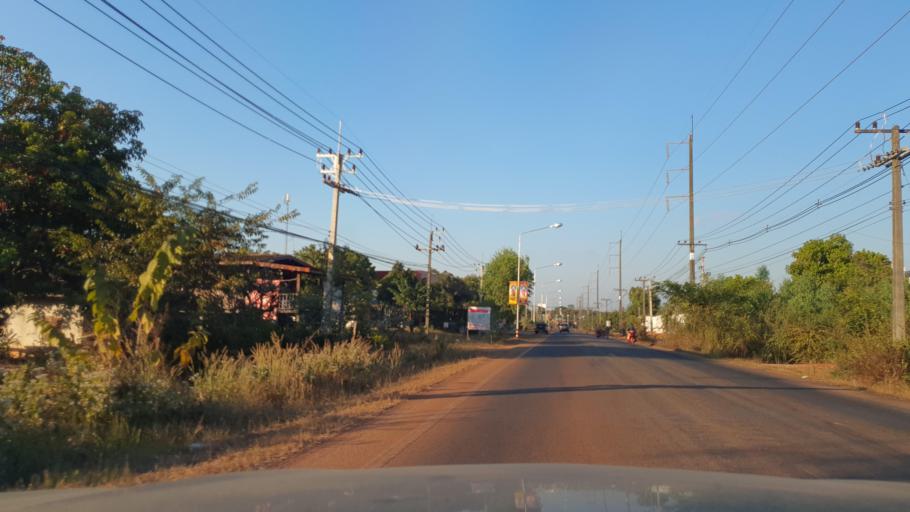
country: TH
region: Nakhon Phanom
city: Si Songkhram
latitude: 17.5810
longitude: 104.2329
